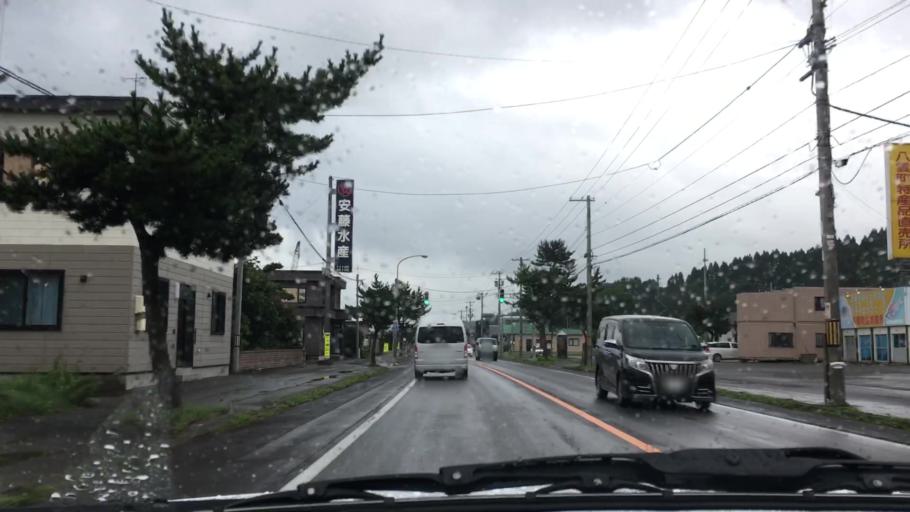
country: JP
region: Hokkaido
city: Nanae
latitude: 42.2318
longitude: 140.3261
